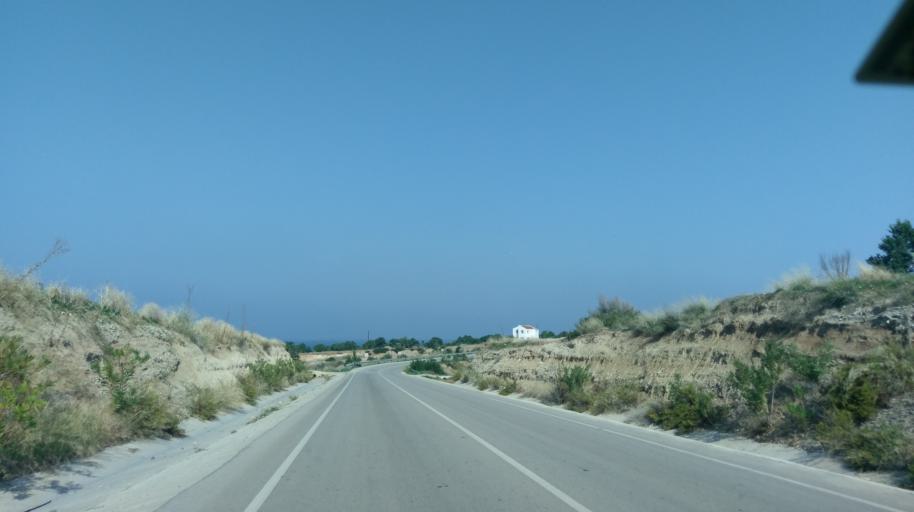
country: CY
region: Ammochostos
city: Lefkonoiko
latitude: 35.3809
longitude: 33.7200
